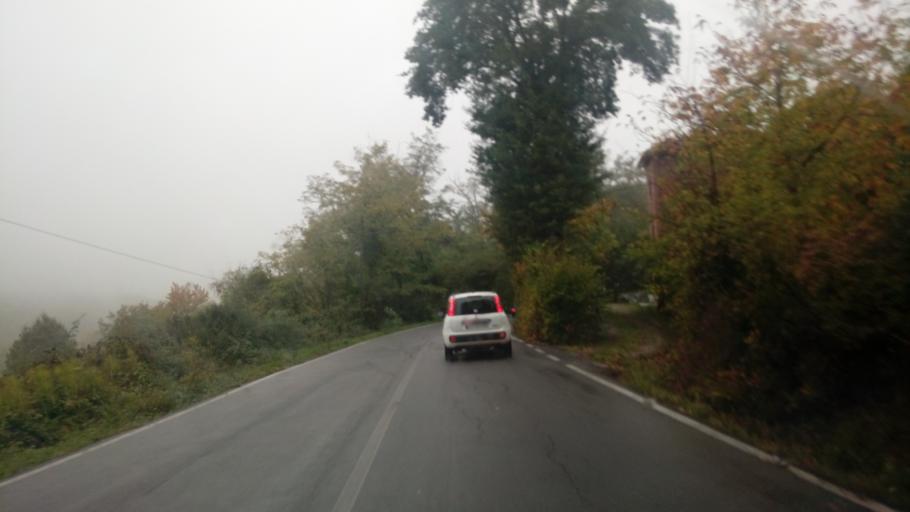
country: IT
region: Emilia-Romagna
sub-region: Provincia di Reggio Emilia
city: Viano
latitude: 44.5462
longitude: 10.6425
